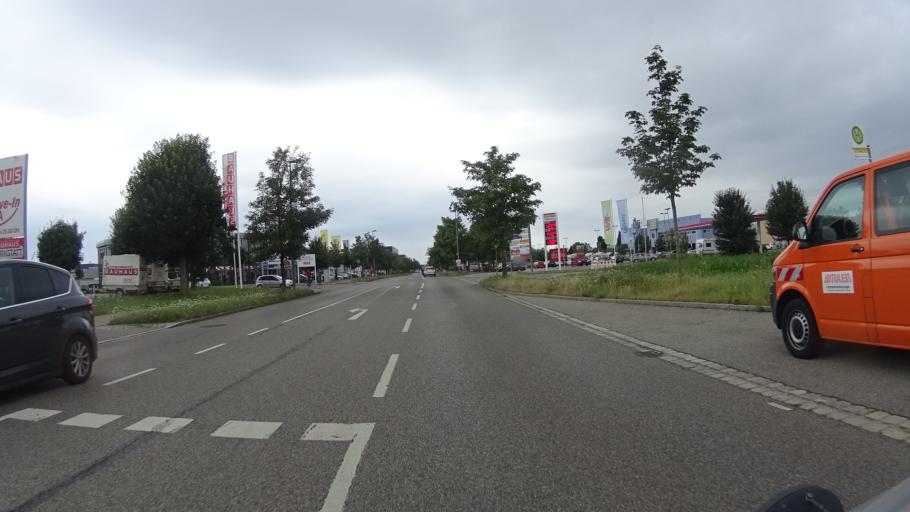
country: DE
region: Bavaria
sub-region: Swabia
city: Memmingen
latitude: 48.0039
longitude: 10.1710
